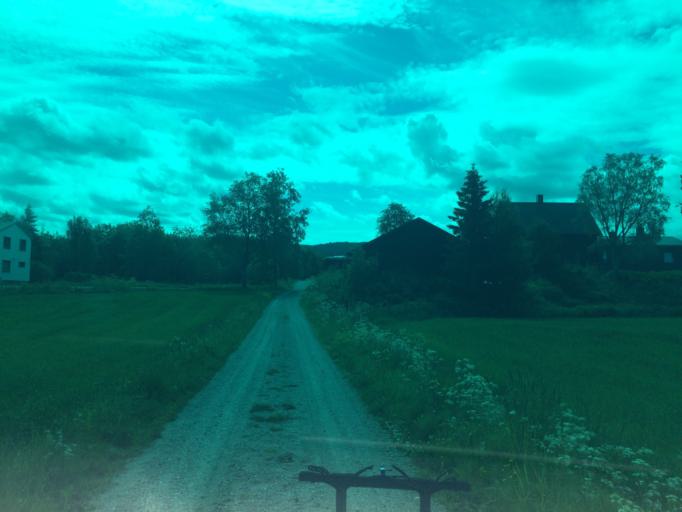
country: NO
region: Nord-Trondelag
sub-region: Overhalla
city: Ranemsletta
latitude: 64.4659
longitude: 12.0609
